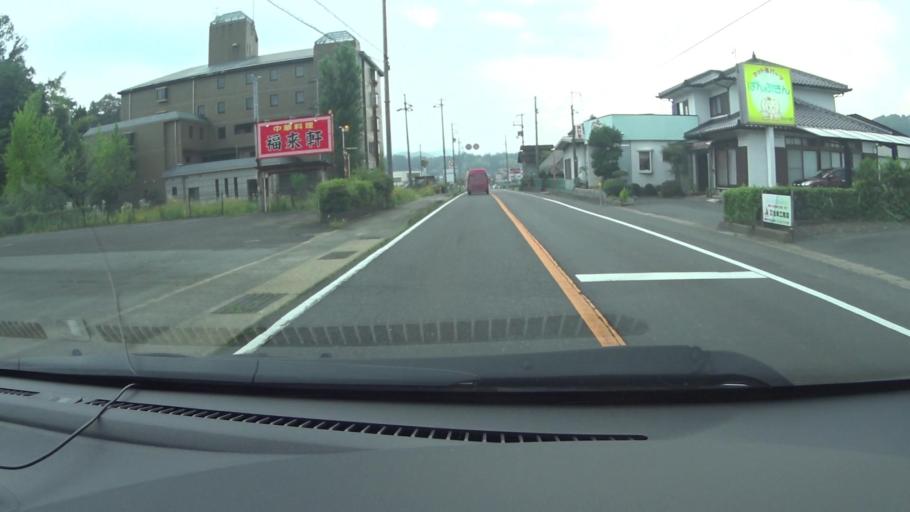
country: JP
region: Kyoto
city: Ayabe
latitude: 35.3167
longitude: 135.2847
